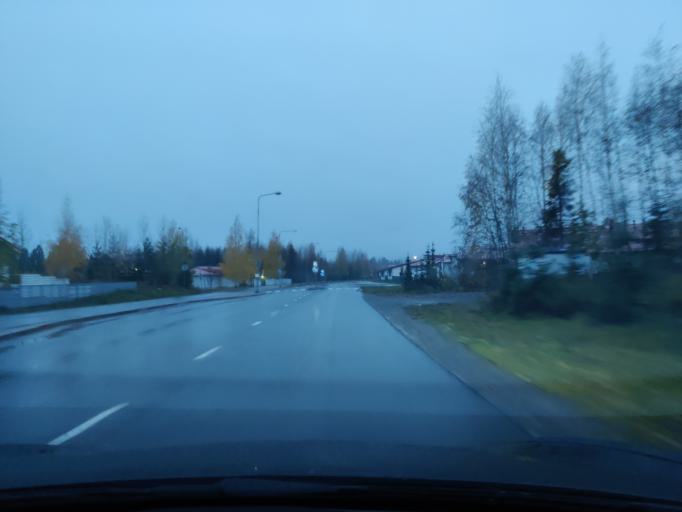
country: FI
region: Northern Savo
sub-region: Kuopio
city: Kuopio
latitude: 62.8265
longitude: 27.6983
